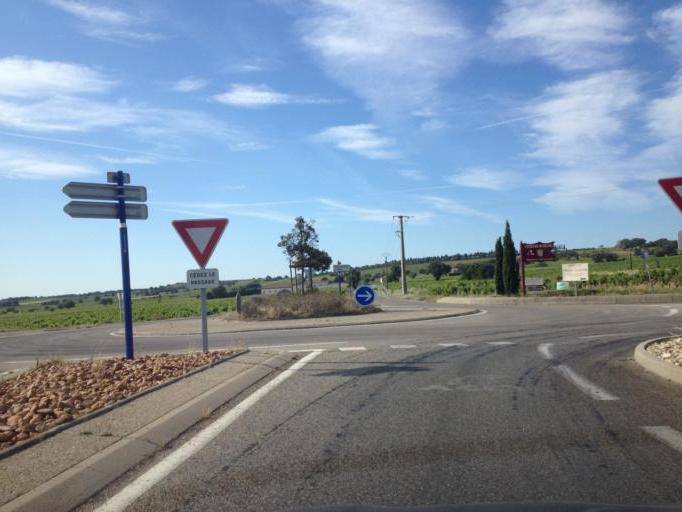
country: FR
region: Provence-Alpes-Cote d'Azur
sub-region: Departement du Vaucluse
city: Chateauneuf-du-Pape
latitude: 44.0966
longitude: 4.8252
